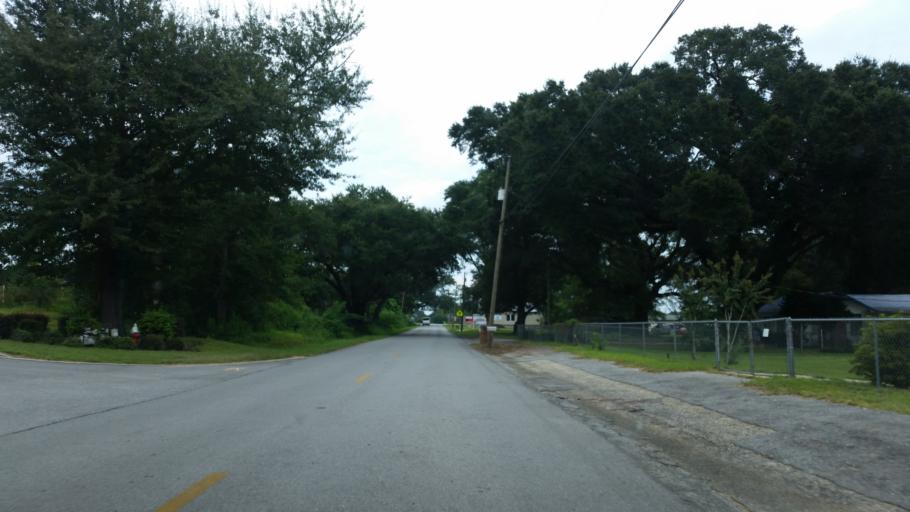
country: US
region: Florida
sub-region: Santa Rosa County
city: Pace
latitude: 30.6040
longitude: -87.1575
